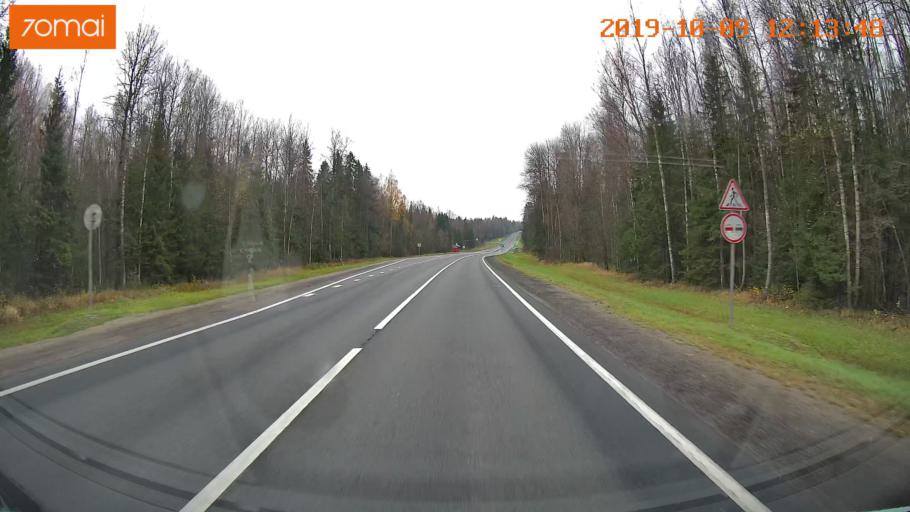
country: RU
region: Jaroslavl
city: Prechistoye
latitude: 58.5050
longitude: 40.3437
